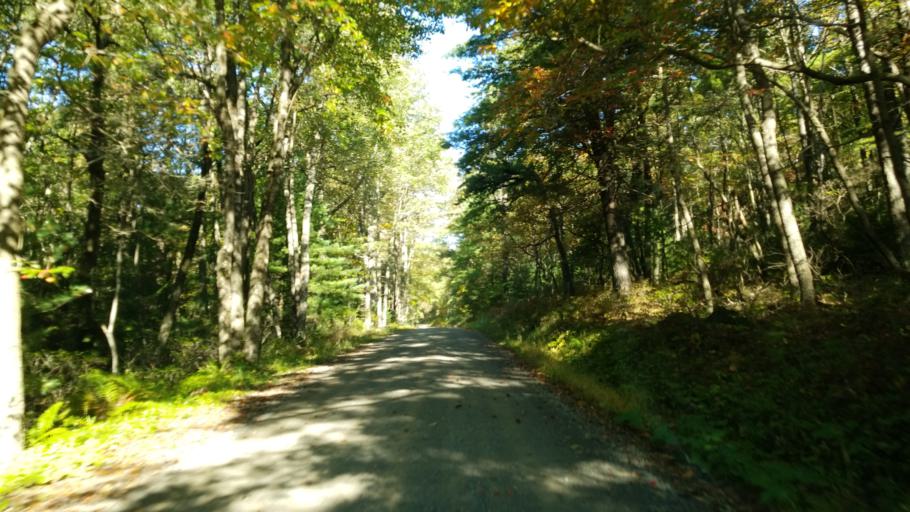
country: US
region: Pennsylvania
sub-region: Clearfield County
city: Hyde
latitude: 41.0834
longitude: -78.5259
